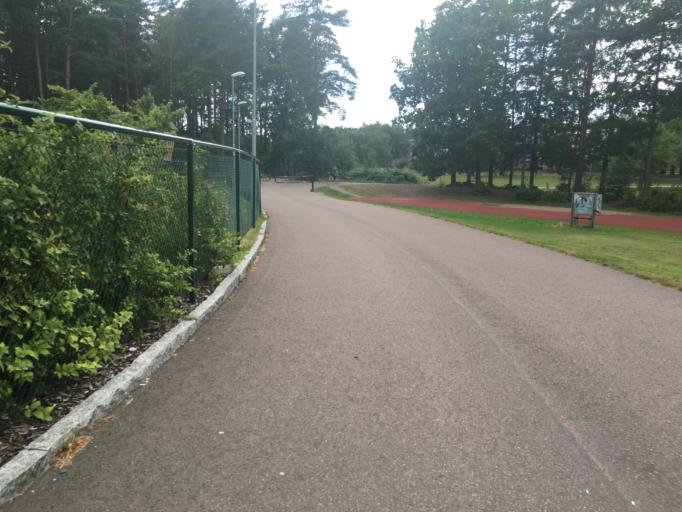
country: SE
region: Kalmar
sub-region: Kalmar Kommun
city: Kalmar
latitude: 56.7021
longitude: 16.3556
